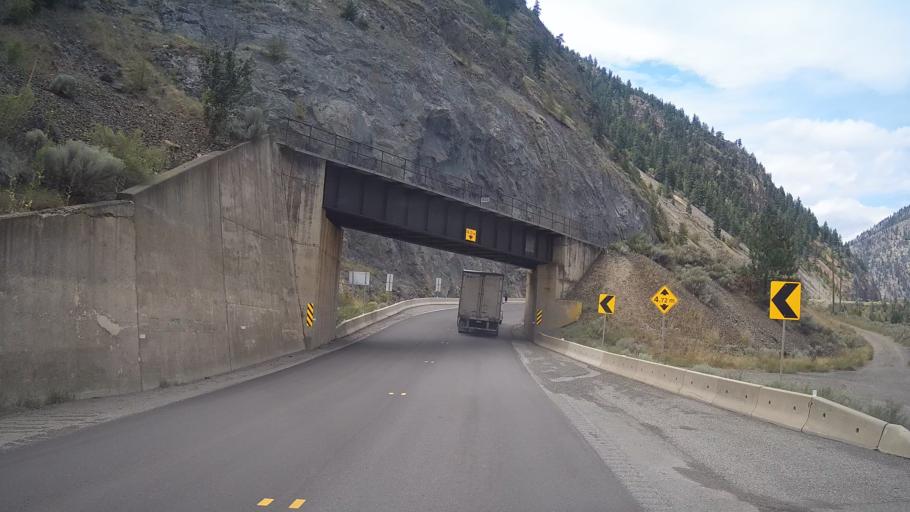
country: CA
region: British Columbia
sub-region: Thompson-Nicola Regional District
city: Ashcroft
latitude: 50.2550
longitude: -121.4459
